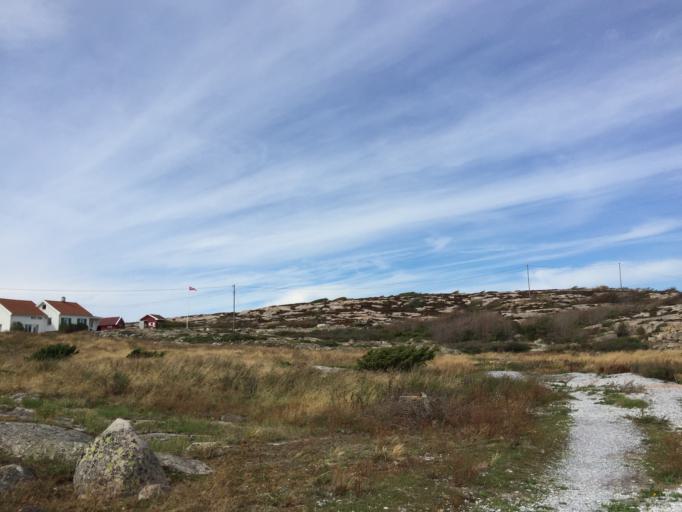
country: NO
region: Ostfold
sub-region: Hvaler
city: Skjaerhalden
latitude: 59.0340
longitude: 10.9475
